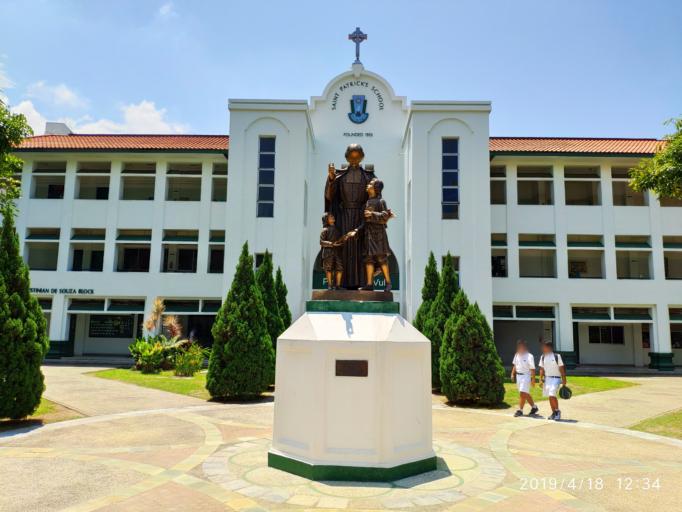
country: SG
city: Singapore
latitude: 1.3085
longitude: 103.9165
